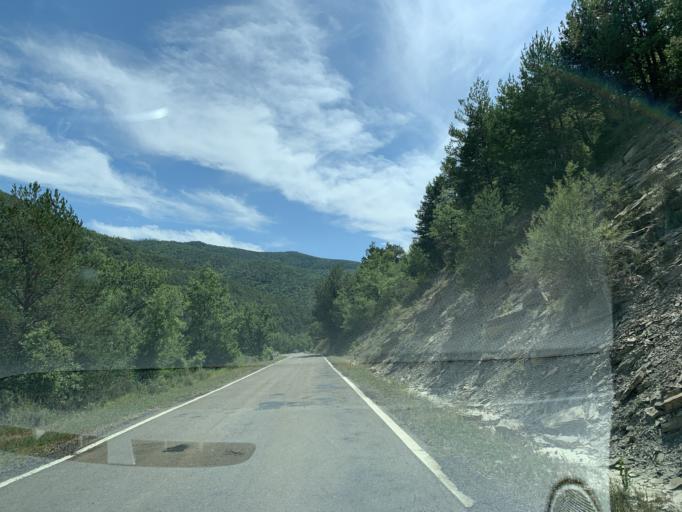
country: ES
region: Aragon
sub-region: Provincia de Huesca
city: Jasa
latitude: 42.6379
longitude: -0.6463
